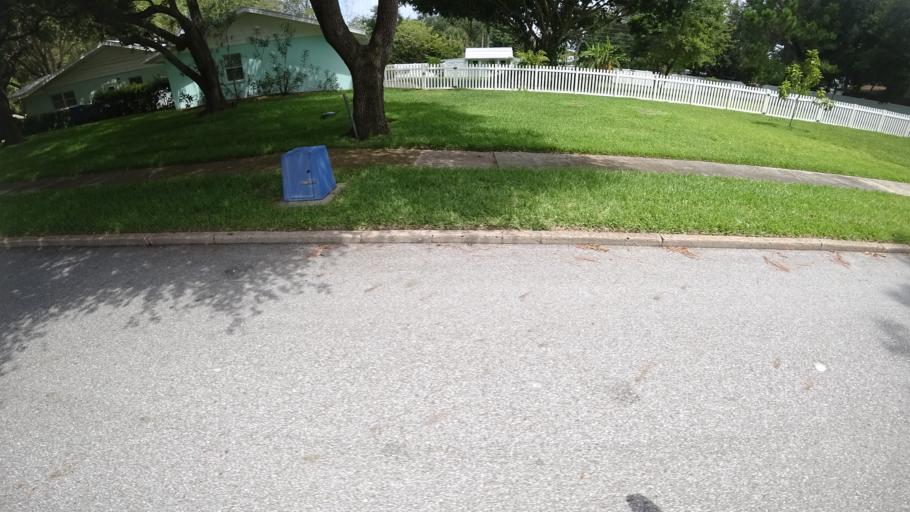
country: US
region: Florida
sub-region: Manatee County
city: Whitfield
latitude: 27.4107
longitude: -82.5754
